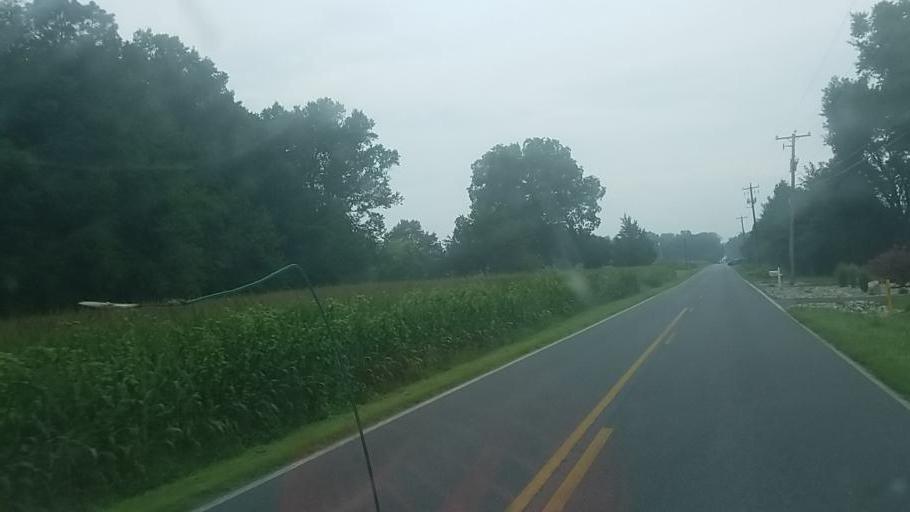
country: US
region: Maryland
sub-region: Wicomico County
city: Salisbury
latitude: 38.3896
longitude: -75.5298
